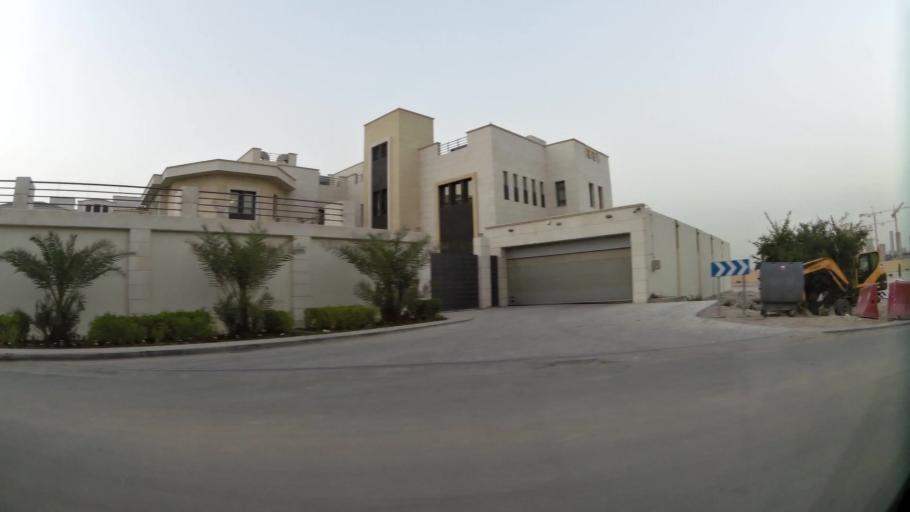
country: QA
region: Baladiyat ar Rayyan
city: Ar Rayyan
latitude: 25.2541
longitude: 51.4662
